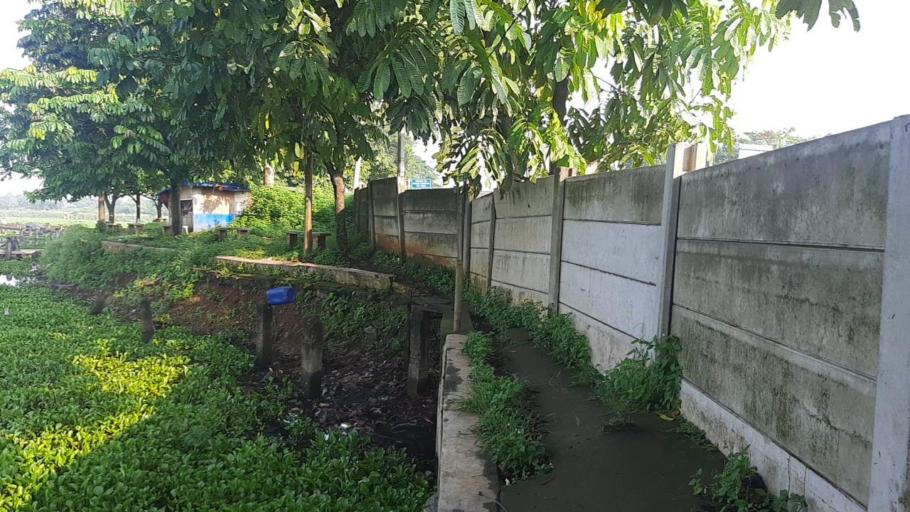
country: ID
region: West Java
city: Citeureup
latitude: -6.4629
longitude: 106.8910
